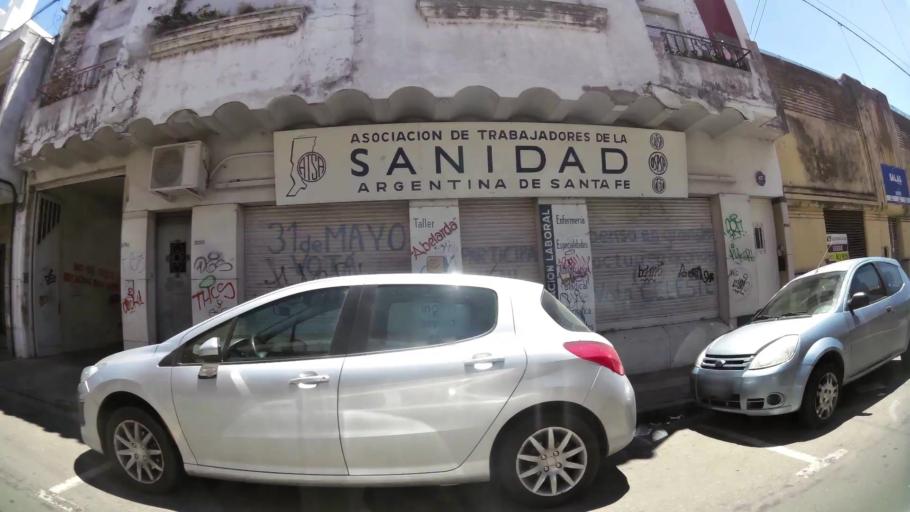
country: AR
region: Santa Fe
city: Santa Fe de la Vera Cruz
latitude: -31.6432
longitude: -60.7096
